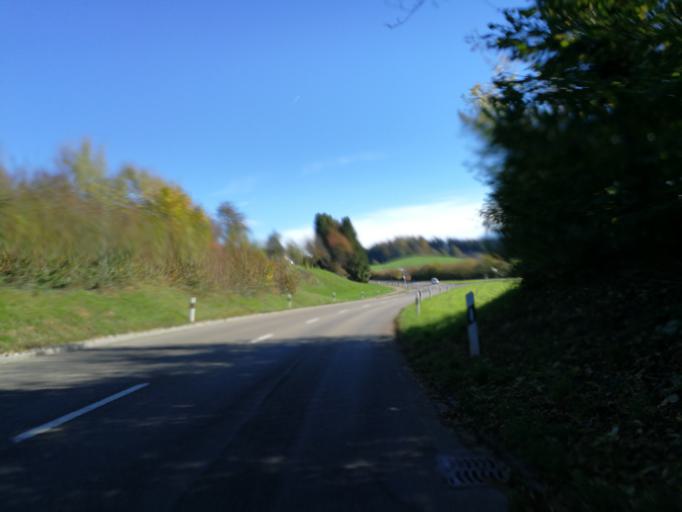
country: CH
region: Zurich
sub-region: Bezirk Uster
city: Moenchaltorf / Dorf
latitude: 47.2896
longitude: 8.7343
